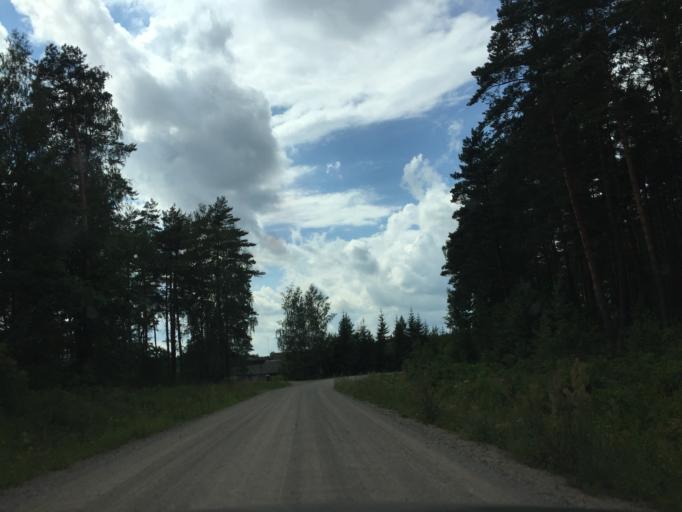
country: LV
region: Jelgava
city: Jelgava
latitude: 56.6243
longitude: 23.6383
